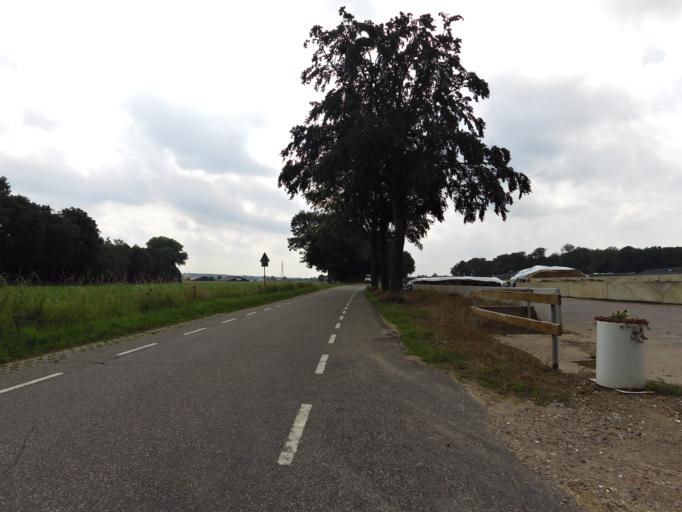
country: NL
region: Gelderland
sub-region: Gemeente Doetinchem
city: Doetinchem
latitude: 51.9472
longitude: 6.2040
